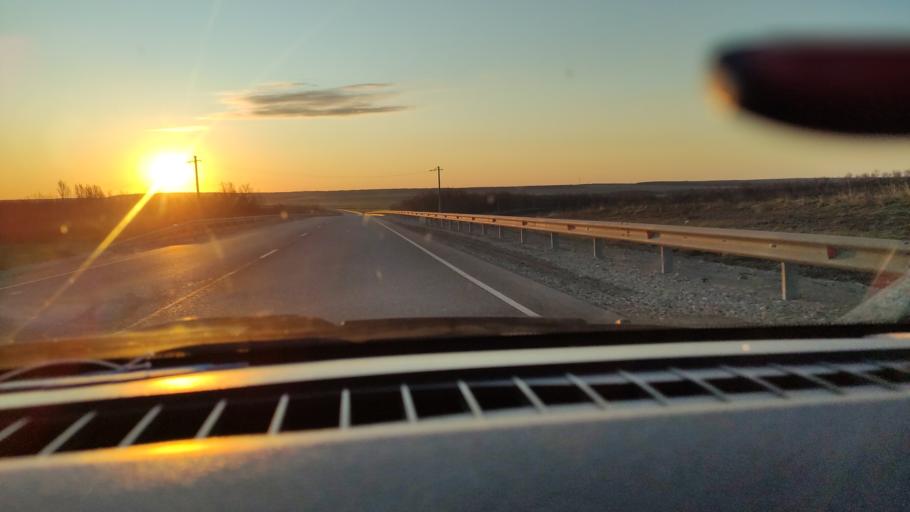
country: RU
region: Saratov
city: Yelshanka
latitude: 51.8308
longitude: 46.4457
